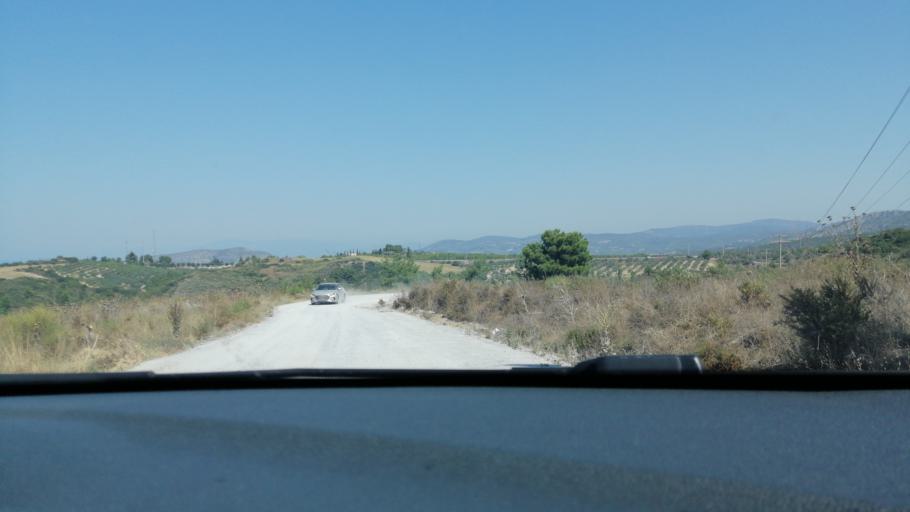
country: TR
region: Aydin
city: Davutlar
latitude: 37.7781
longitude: 27.3142
